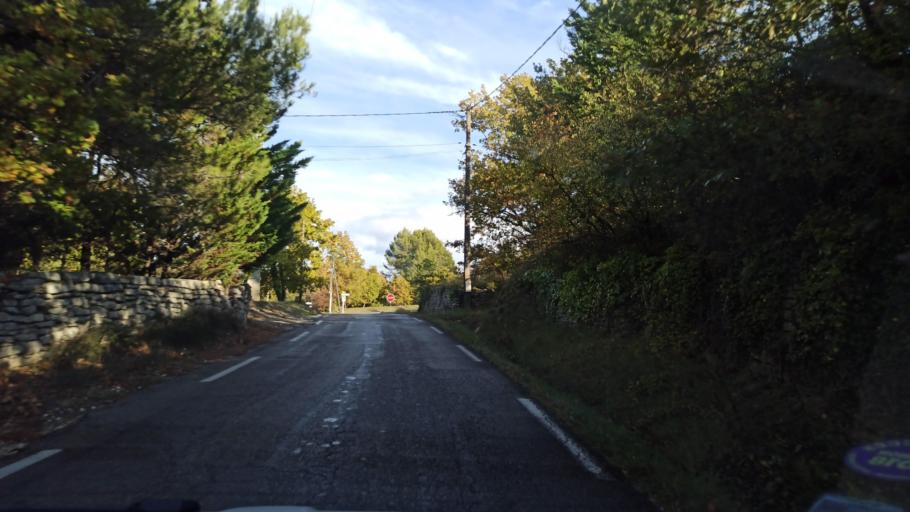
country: FR
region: Provence-Alpes-Cote d'Azur
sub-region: Departement du Vaucluse
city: Goult
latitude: 43.8367
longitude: 5.2682
